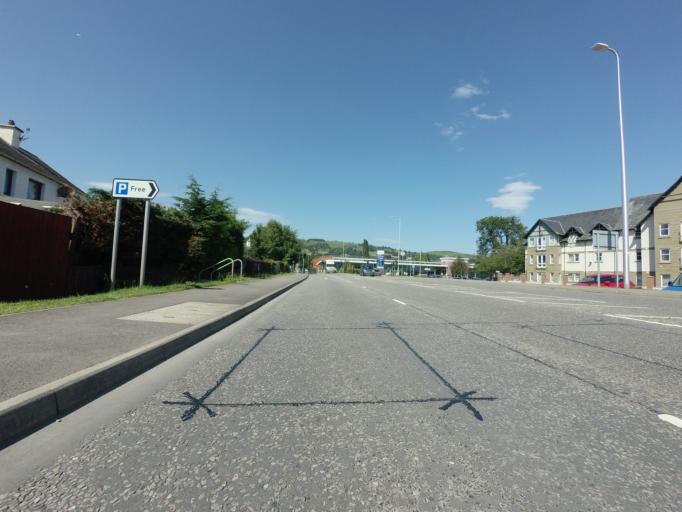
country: GB
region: Scotland
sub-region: Highland
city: Dingwall
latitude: 57.5962
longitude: -4.4315
